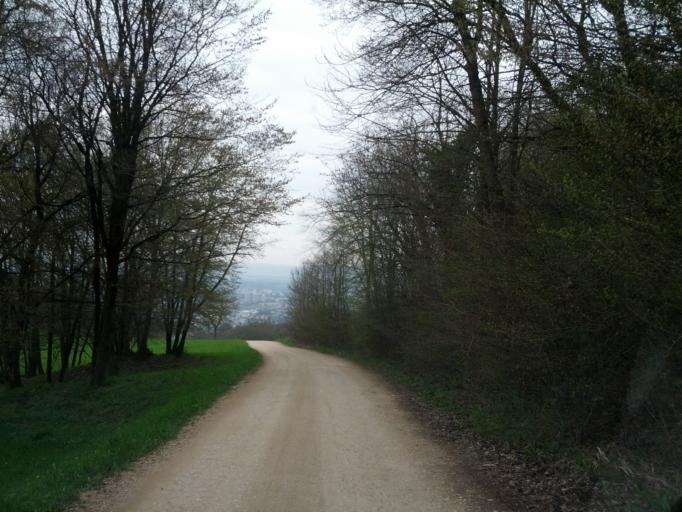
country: DE
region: Baden-Wuerttemberg
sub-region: Freiburg Region
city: Wittnau
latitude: 47.9578
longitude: 7.7999
